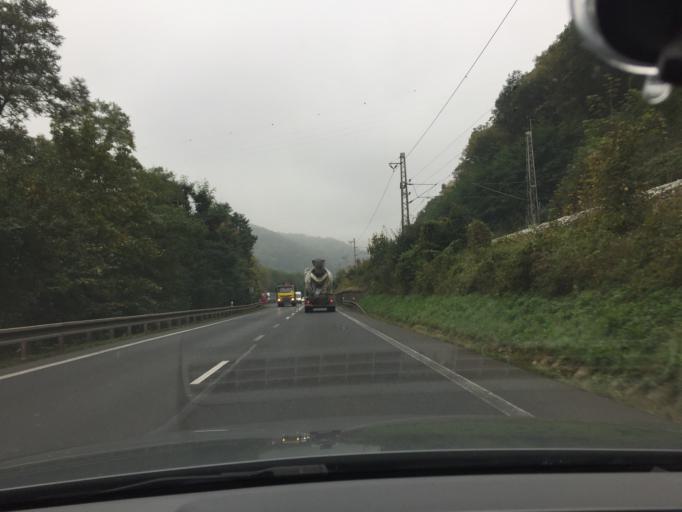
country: CZ
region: Ustecky
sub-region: Okres Usti nad Labem
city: Usti nad Labem
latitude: 50.6189
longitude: 14.0736
